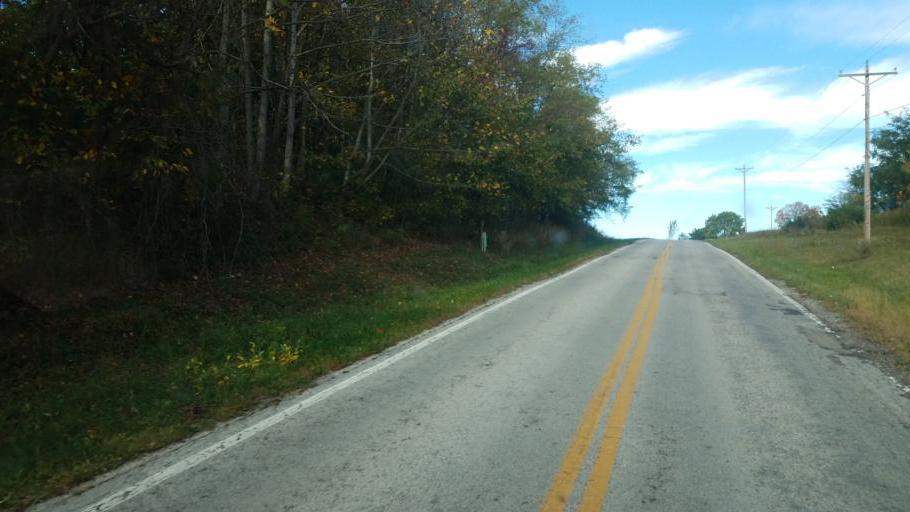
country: US
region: Ohio
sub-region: Huron County
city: Greenwich
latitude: 41.1032
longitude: -82.4872
